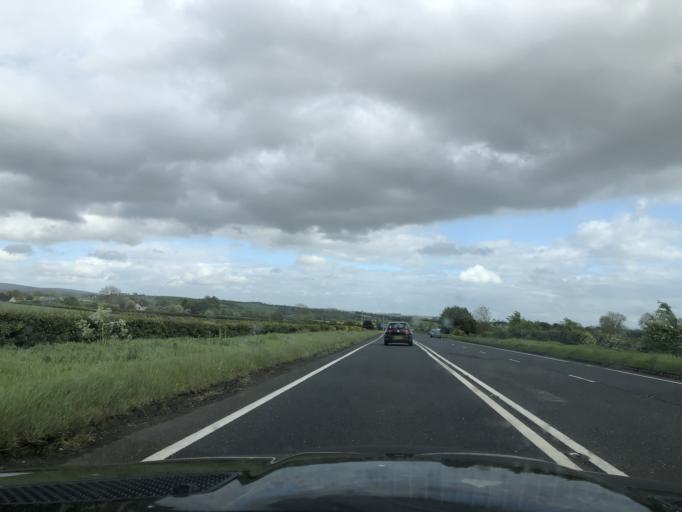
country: GB
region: Northern Ireland
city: Dunloy
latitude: 55.0279
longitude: -6.3921
